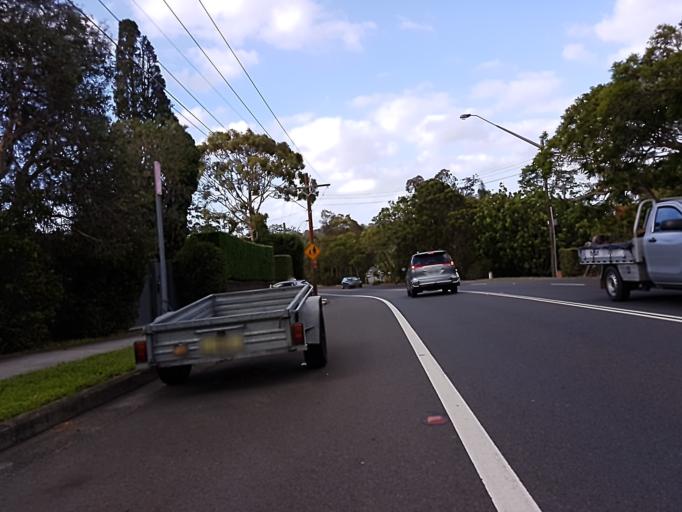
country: AU
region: New South Wales
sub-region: Manly Vale
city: Balgowlah
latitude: -33.7905
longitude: 151.2413
